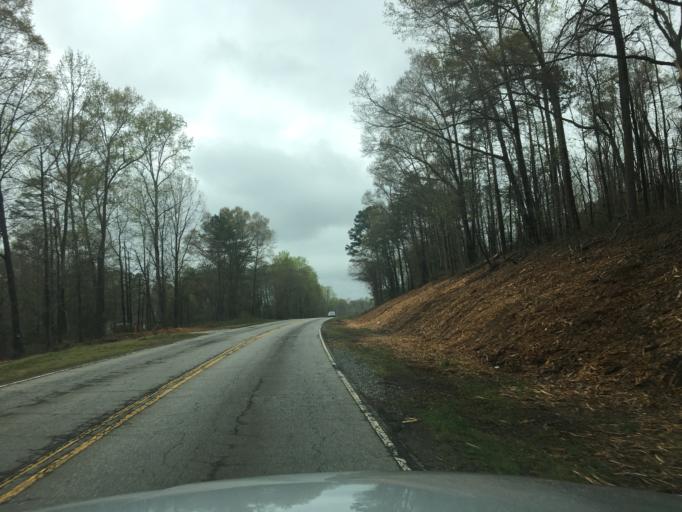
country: US
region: South Carolina
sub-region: Spartanburg County
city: Wellford
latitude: 34.9624
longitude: -82.0836
